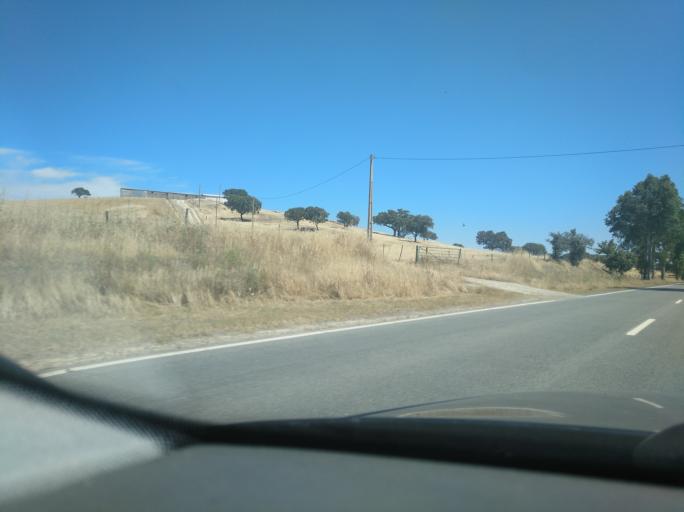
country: PT
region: Beja
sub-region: Castro Verde
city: Castro Verde
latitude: 37.6755
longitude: -8.0825
